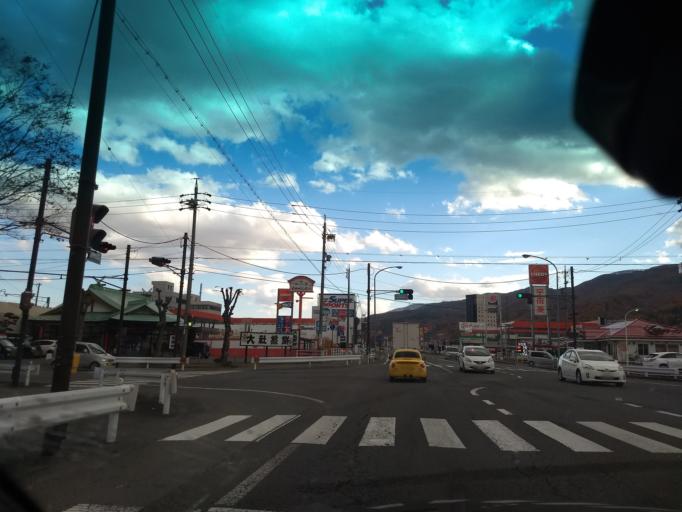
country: JP
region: Nagano
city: Chino
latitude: 36.0056
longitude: 138.1315
